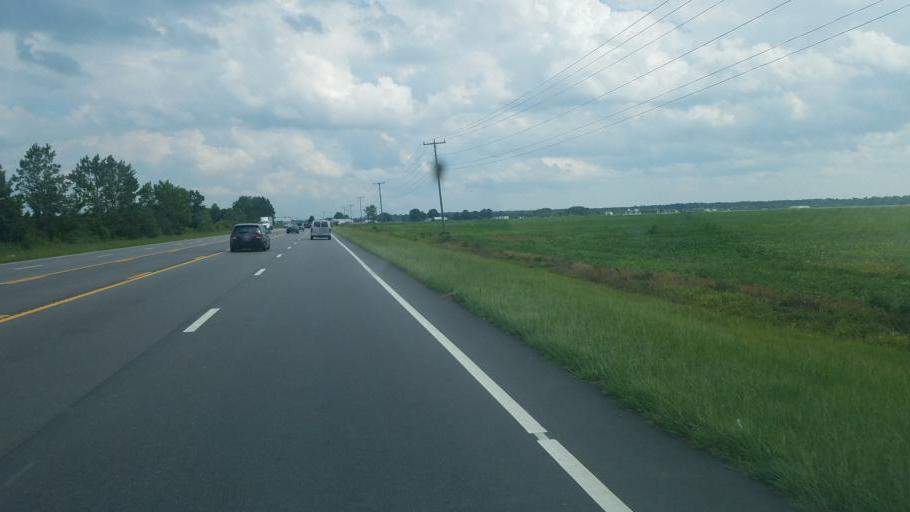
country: US
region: North Carolina
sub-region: Currituck County
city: Moyock
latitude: 36.5130
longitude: -76.1649
